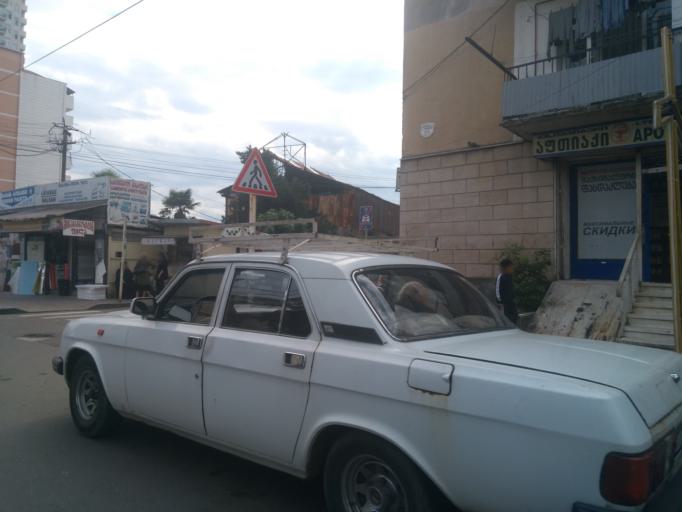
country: GE
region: Ajaria
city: Batumi
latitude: 41.6436
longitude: 41.6450
